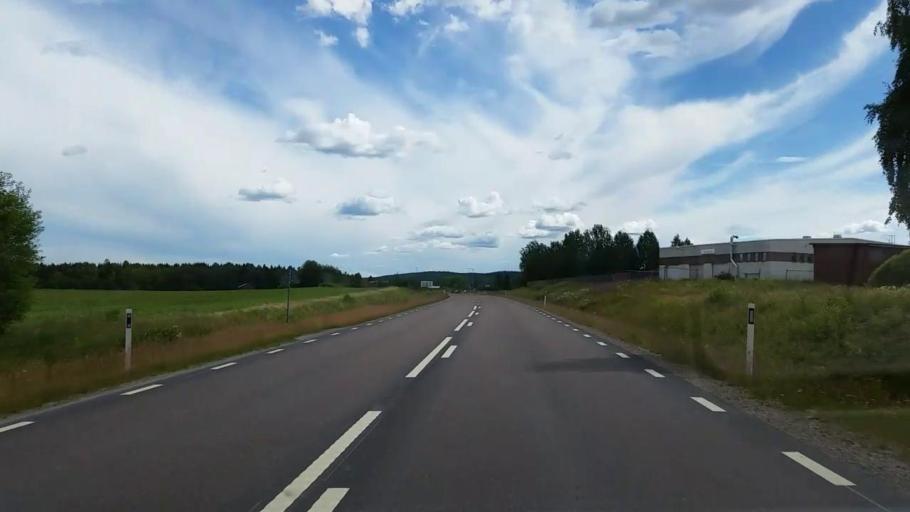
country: SE
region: Gaevleborg
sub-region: Ovanakers Kommun
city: Edsbyn
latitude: 61.3754
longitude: 15.8414
